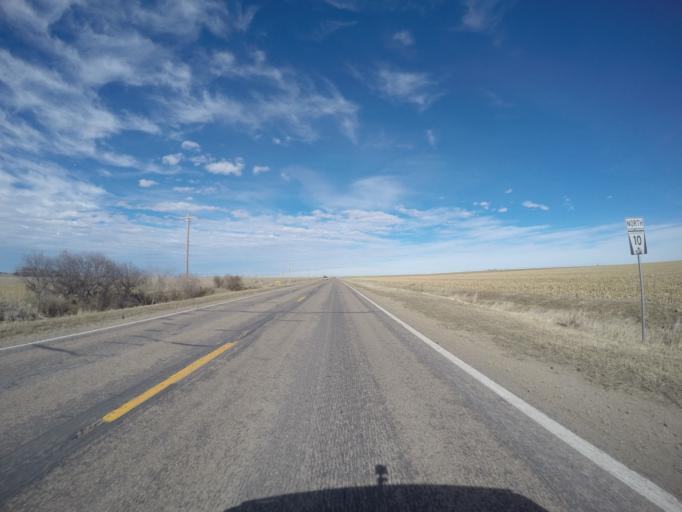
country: US
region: Nebraska
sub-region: Franklin County
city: Franklin
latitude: 40.2081
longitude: -98.9524
